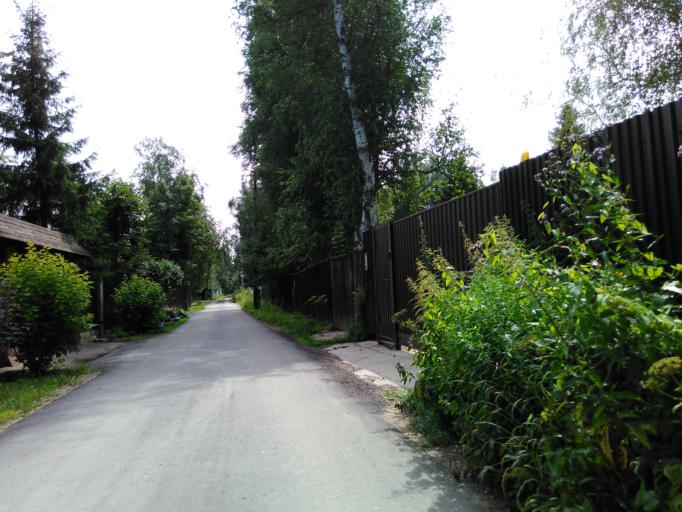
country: RU
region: Moskovskaya
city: Pravdinskiy
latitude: 56.0598
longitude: 37.8391
